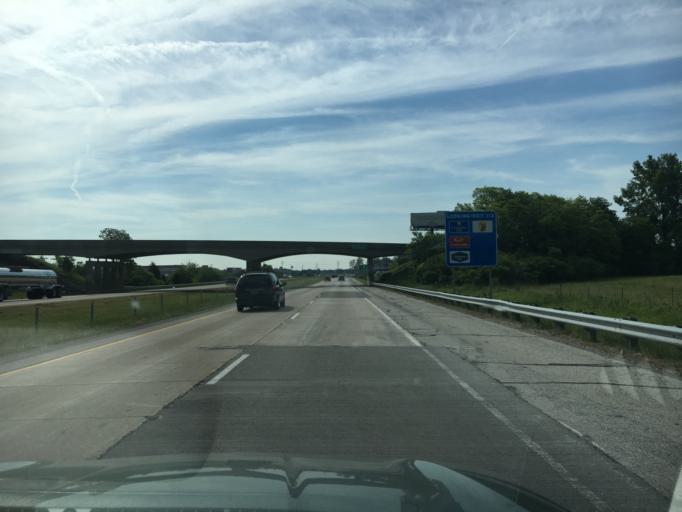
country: US
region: Indiana
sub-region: Shelby County
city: Shelbyville
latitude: 39.5649
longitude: -85.7962
